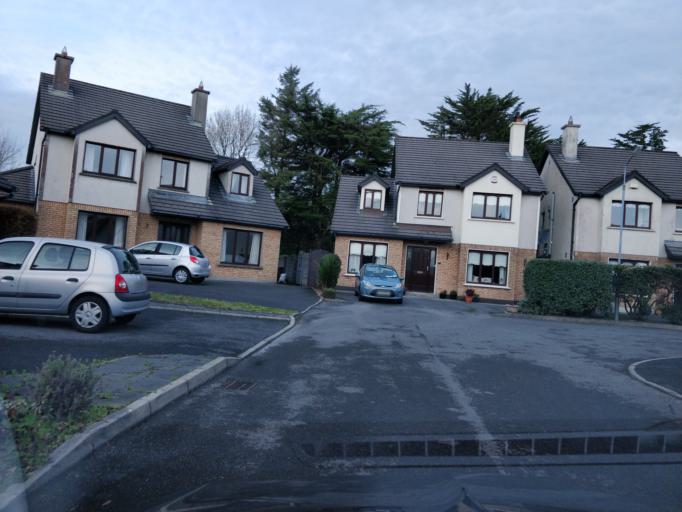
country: IE
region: Connaught
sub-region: County Galway
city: Bearna
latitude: 53.2659
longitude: -9.1075
